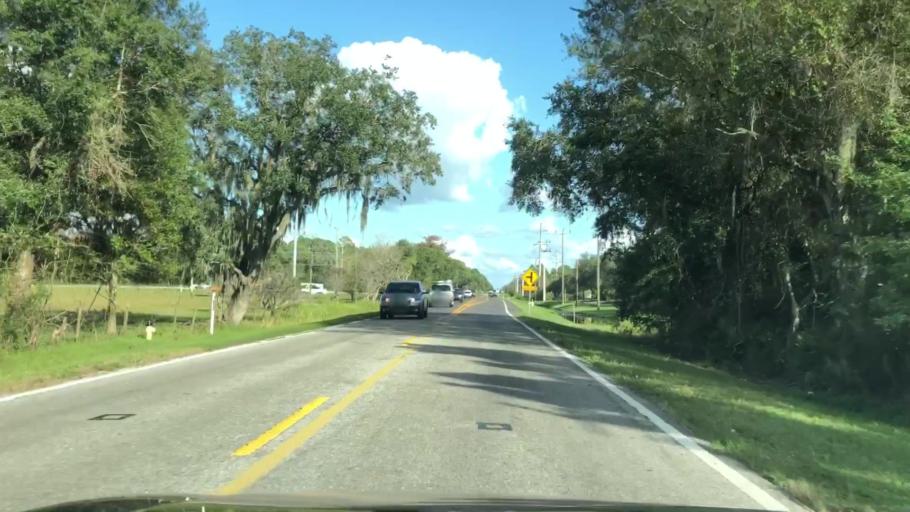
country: US
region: Florida
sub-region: Sarasota County
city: Lake Sarasota
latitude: 27.3386
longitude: -82.3866
